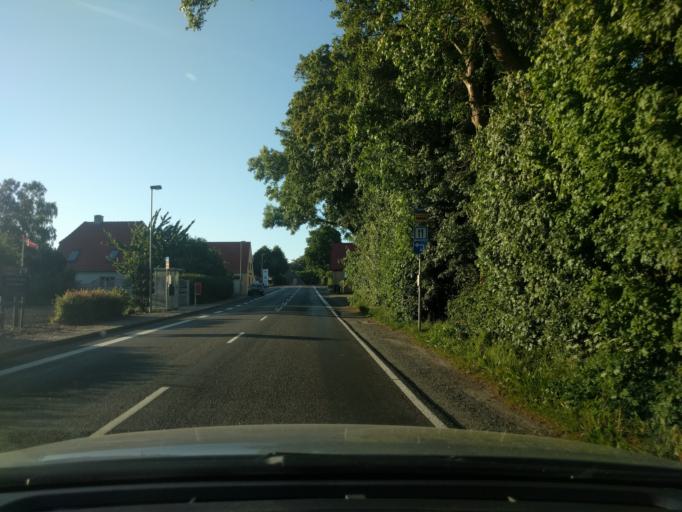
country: DK
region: South Denmark
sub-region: Kerteminde Kommune
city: Kerteminde
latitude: 55.5002
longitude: 10.6495
